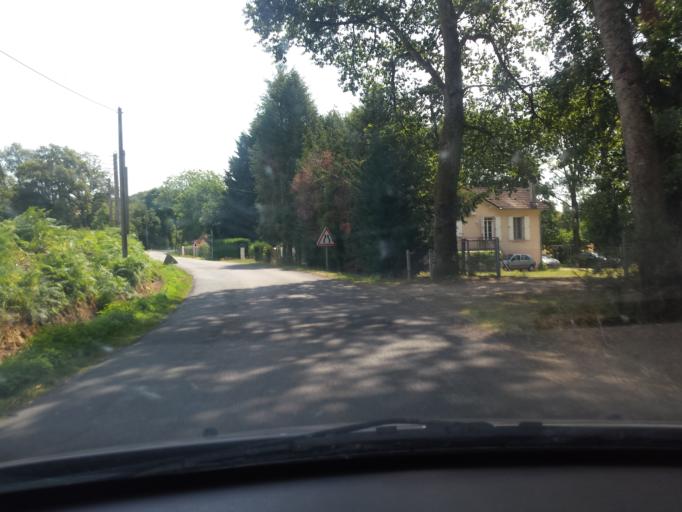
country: FR
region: Poitou-Charentes
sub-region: Departement de la Vienne
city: Availles-Limouzine
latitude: 46.1084
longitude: 0.6831
